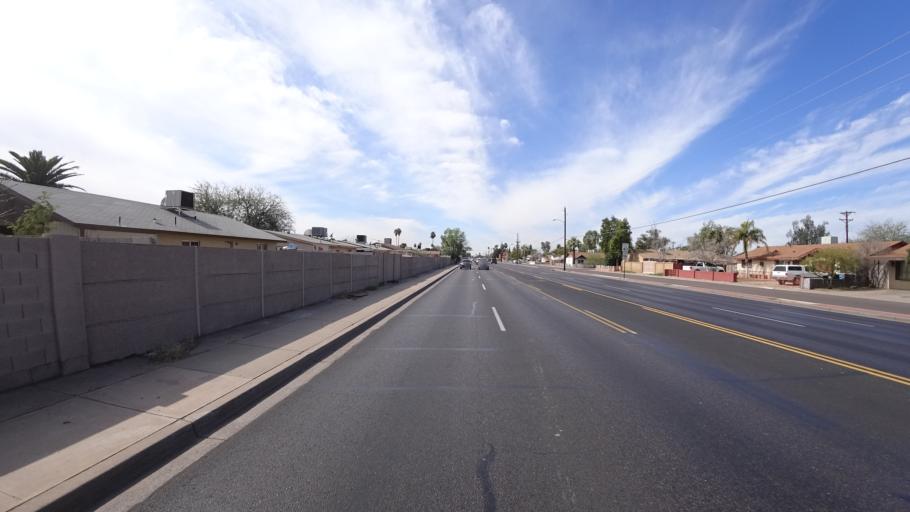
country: US
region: Arizona
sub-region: Maricopa County
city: Glendale
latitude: 33.4805
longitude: -112.1790
